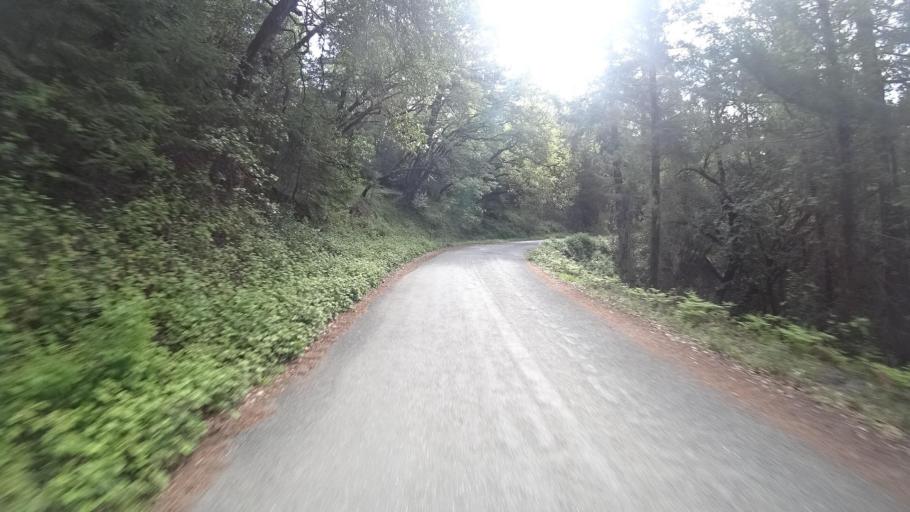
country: US
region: California
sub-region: Humboldt County
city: Redway
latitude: 40.1707
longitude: -123.5657
